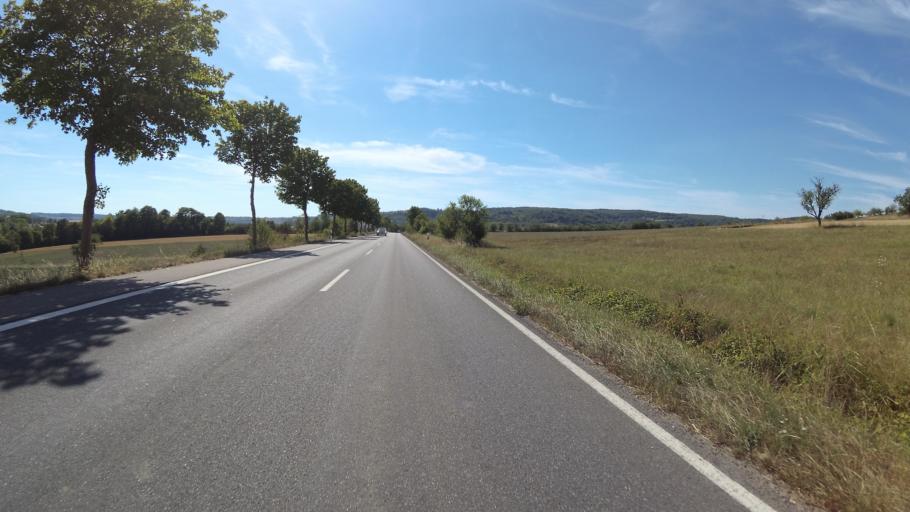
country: DE
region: Saarland
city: Gersheim
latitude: 49.1502
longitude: 7.2220
